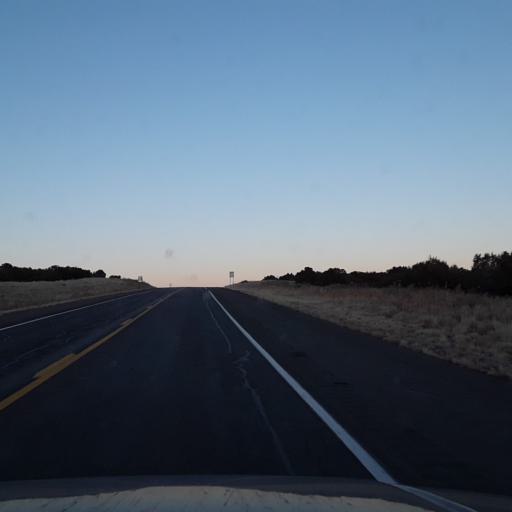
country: US
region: New Mexico
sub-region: Guadalupe County
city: Santa Rosa
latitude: 34.5304
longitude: -105.3211
